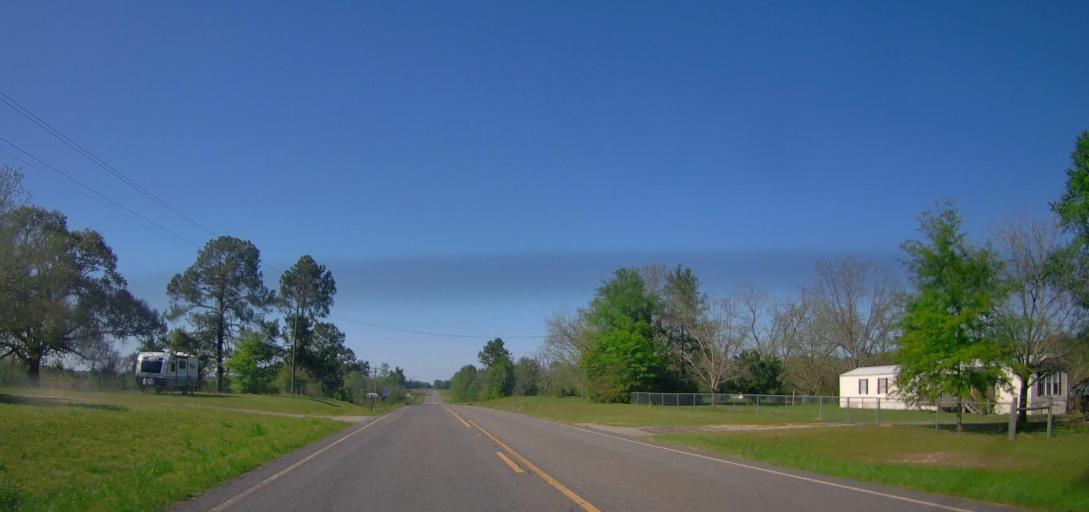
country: US
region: Georgia
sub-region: Wilcox County
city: Rochelle
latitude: 32.0653
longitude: -83.5035
